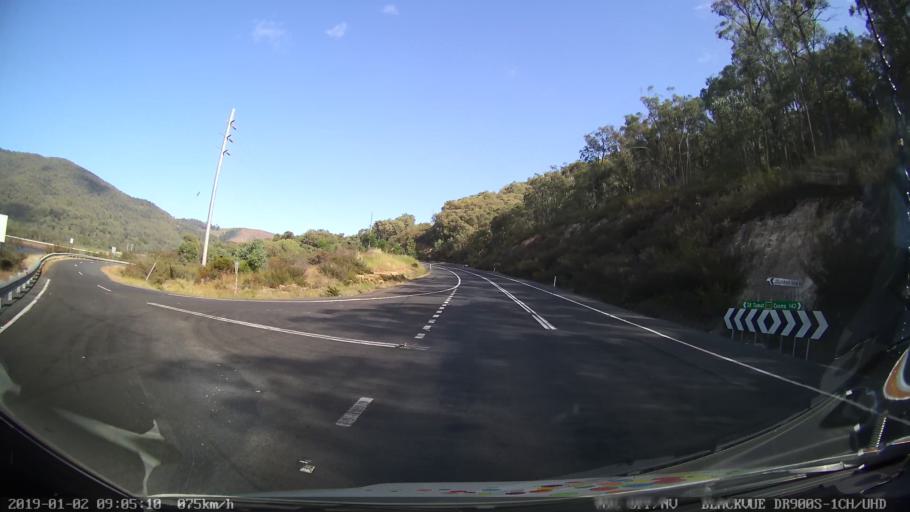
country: AU
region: New South Wales
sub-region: Tumut Shire
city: Tumut
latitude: -35.5624
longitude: 148.3120
